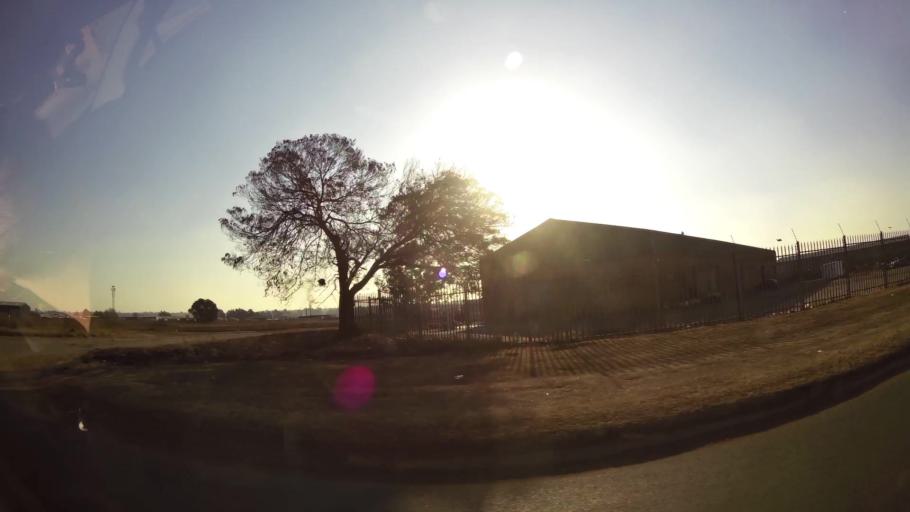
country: ZA
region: Gauteng
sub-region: West Rand District Municipality
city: Randfontein
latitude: -26.1982
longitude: 27.6884
